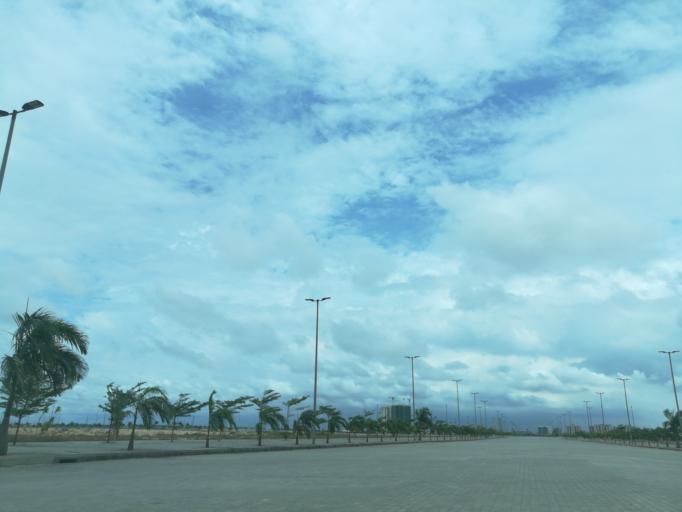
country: NG
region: Lagos
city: Ikoyi
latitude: 6.4094
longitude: 3.4179
